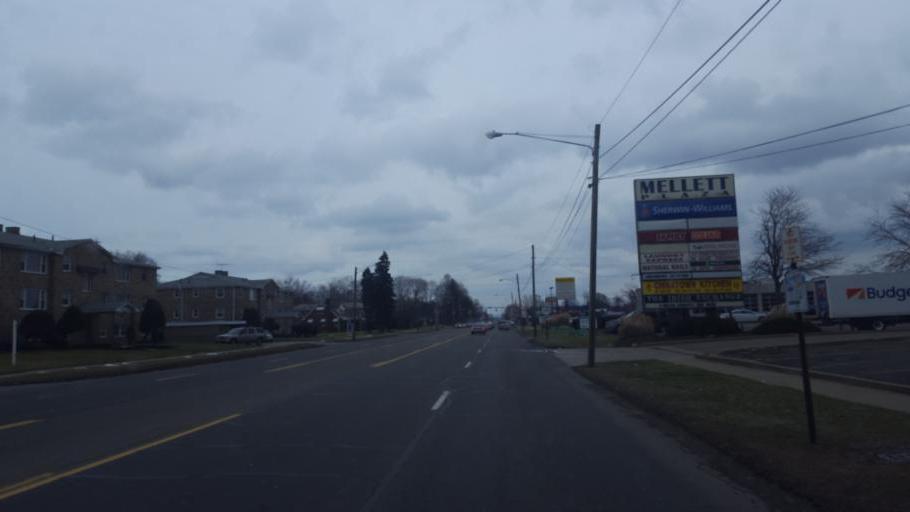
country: US
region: Ohio
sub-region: Stark County
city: Canton
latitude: 40.7971
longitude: -81.4196
